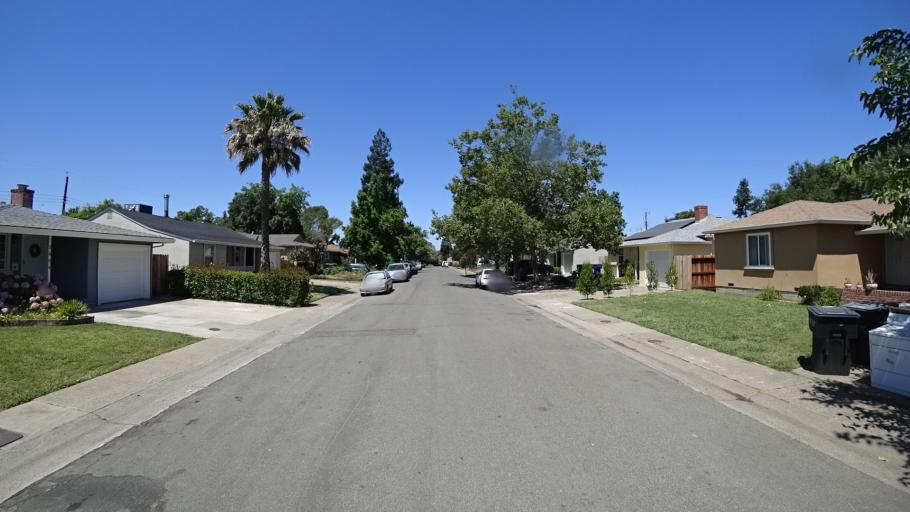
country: US
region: California
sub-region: Sacramento County
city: Parkway
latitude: 38.5362
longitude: -121.4767
